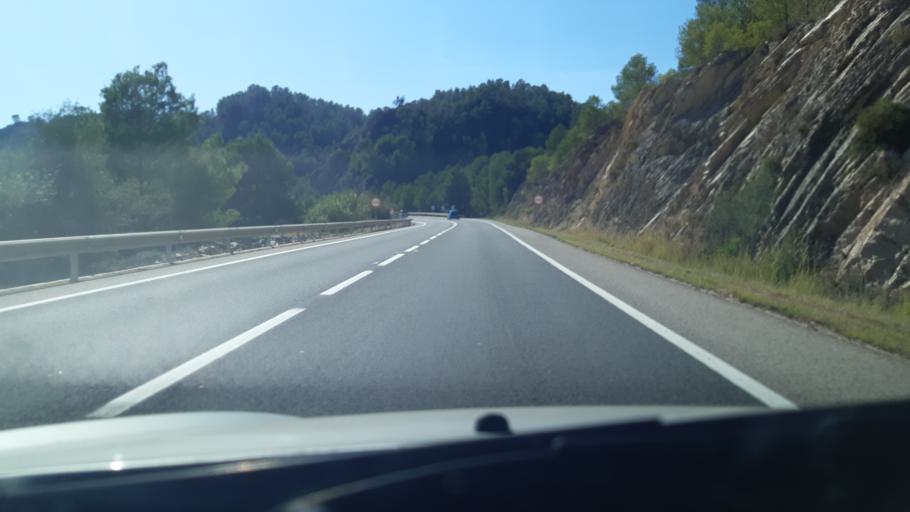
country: ES
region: Catalonia
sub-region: Provincia de Tarragona
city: Benifallet
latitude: 40.9548
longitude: 0.4848
